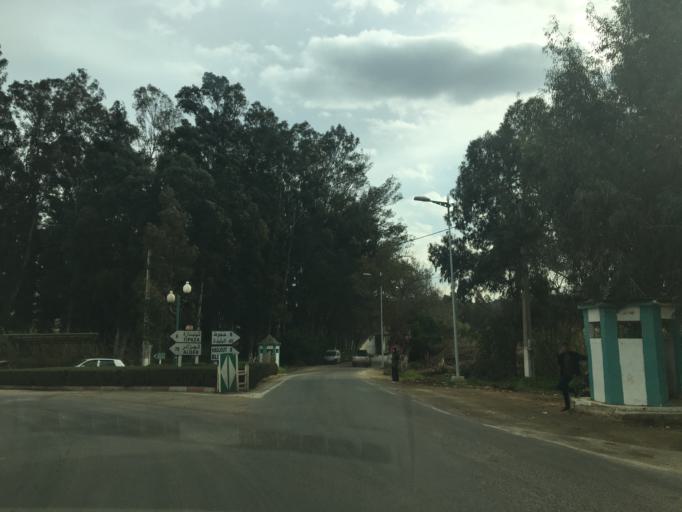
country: DZ
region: Tipaza
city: Hadjout
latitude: 36.5670
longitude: 2.3938
